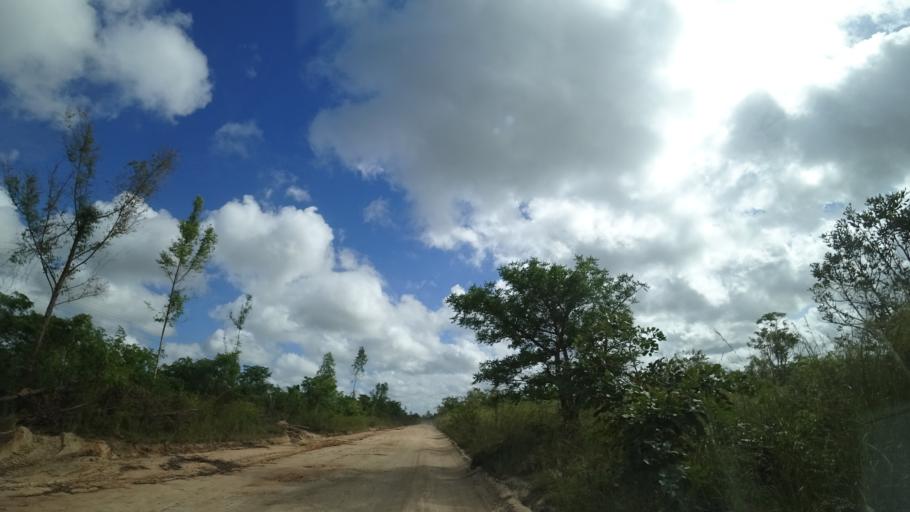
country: MZ
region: Sofala
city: Dondo
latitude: -19.4397
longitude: 34.7144
